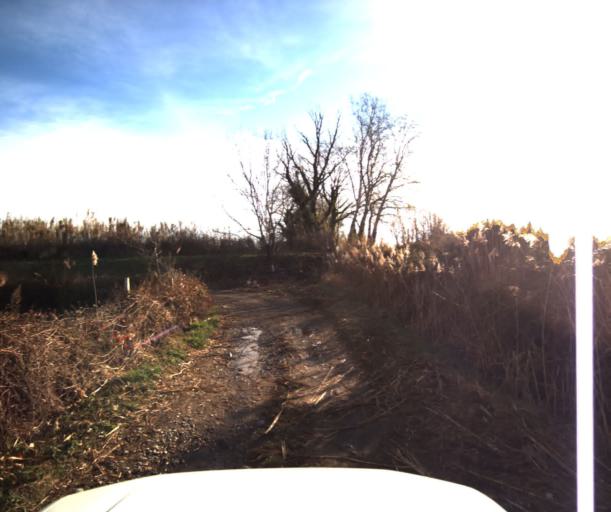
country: FR
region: Provence-Alpes-Cote d'Azur
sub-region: Departement du Vaucluse
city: Pertuis
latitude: 43.6732
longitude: 5.4852
